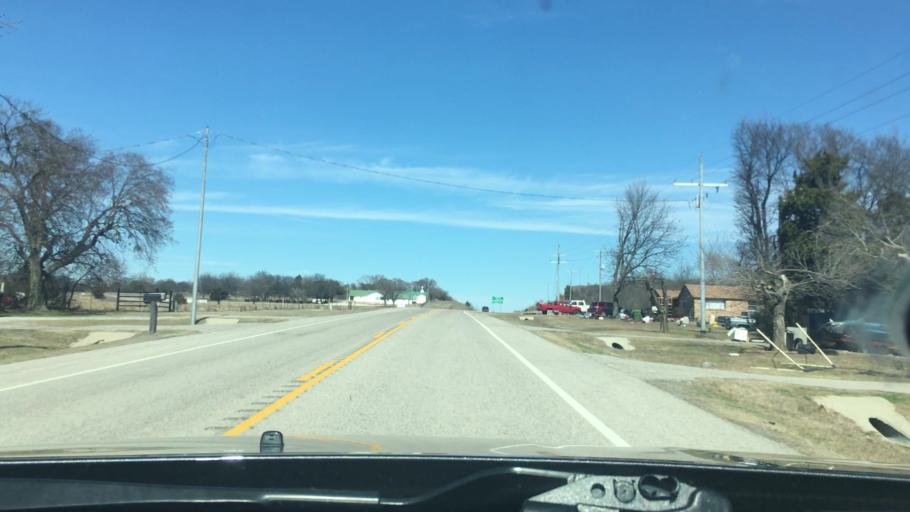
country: US
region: Oklahoma
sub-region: Murray County
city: Sulphur
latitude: 34.4008
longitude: -96.9510
